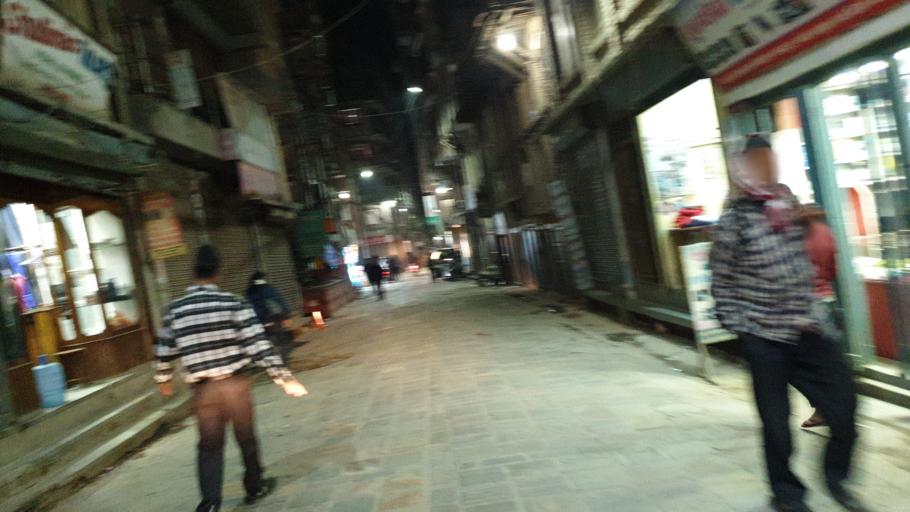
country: NP
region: Central Region
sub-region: Bagmati Zone
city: Kathmandu
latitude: 27.7017
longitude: 85.3078
